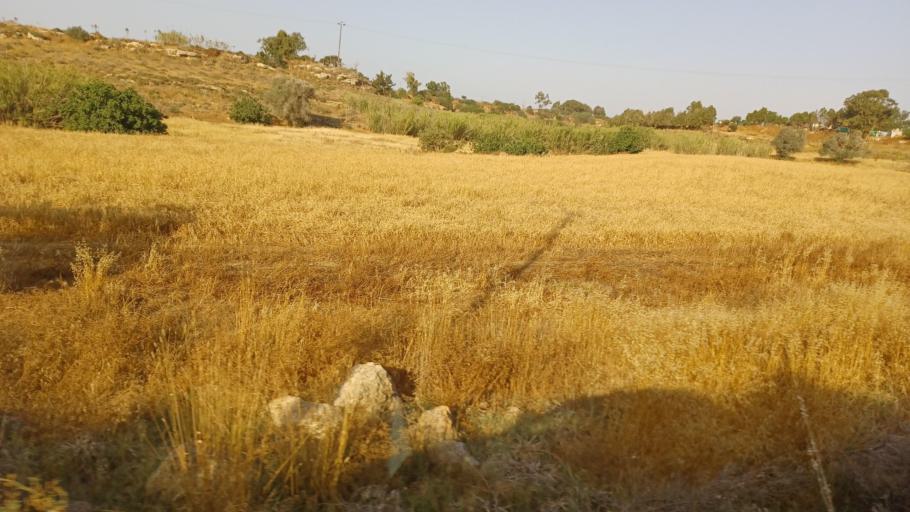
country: CY
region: Ammochostos
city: Liopetri
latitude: 34.9765
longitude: 33.8931
